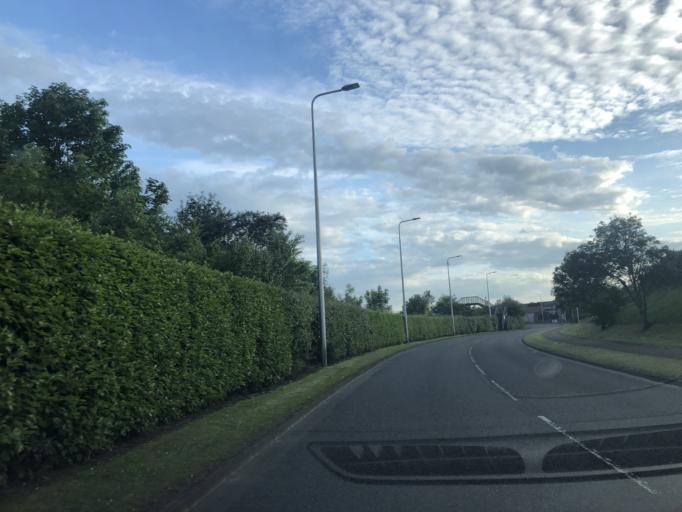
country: GB
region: Scotland
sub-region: Fife
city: Leven
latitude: 56.1875
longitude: -3.0051
